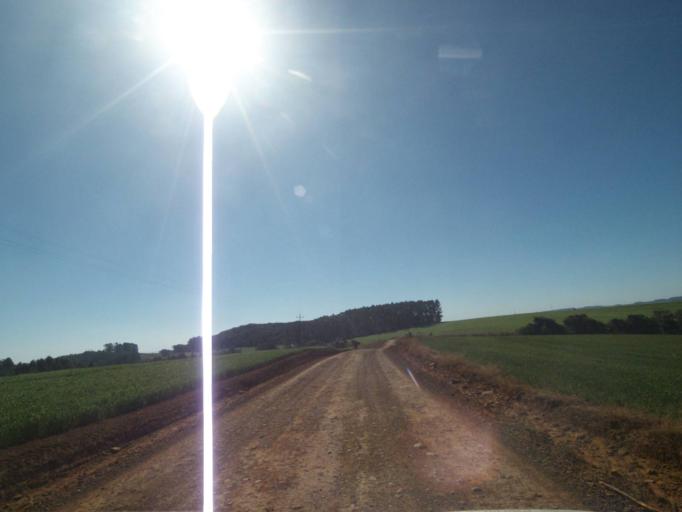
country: BR
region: Parana
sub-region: Tibagi
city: Tibagi
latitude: -24.6016
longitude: -50.6032
